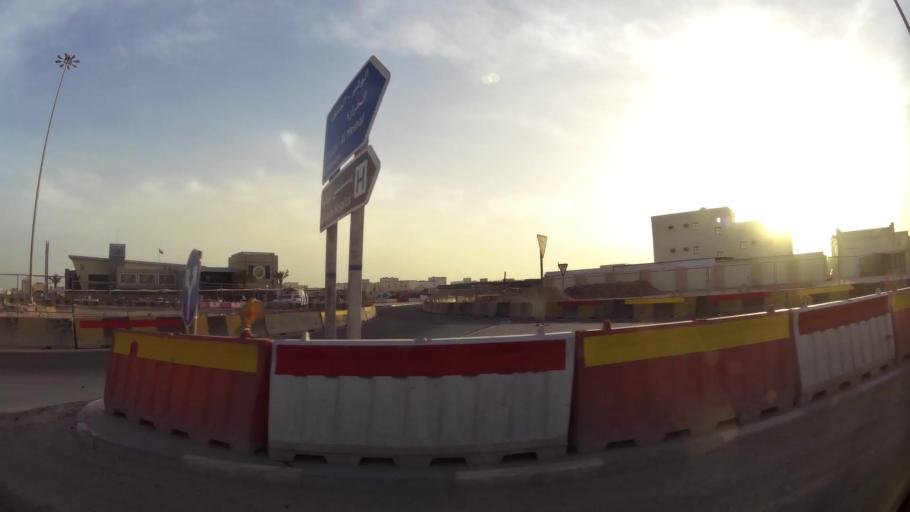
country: QA
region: Al Wakrah
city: Al Wakrah
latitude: 25.1519
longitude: 51.5938
